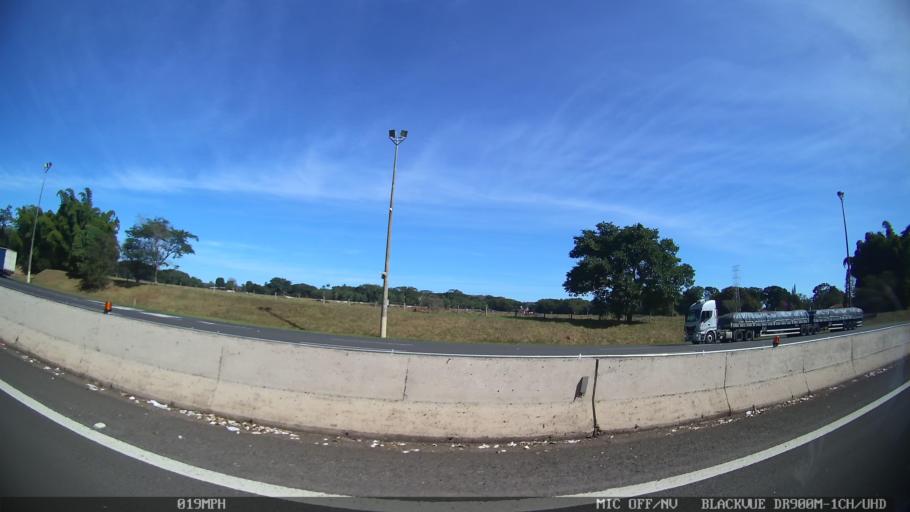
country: BR
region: Sao Paulo
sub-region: Pirassununga
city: Pirassununga
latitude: -21.9564
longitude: -47.4599
